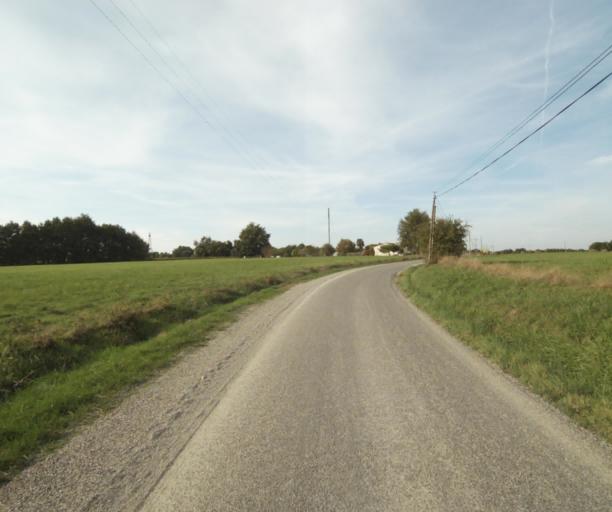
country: FR
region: Midi-Pyrenees
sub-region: Departement du Tarn-et-Garonne
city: Campsas
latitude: 43.9096
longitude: 1.3316
